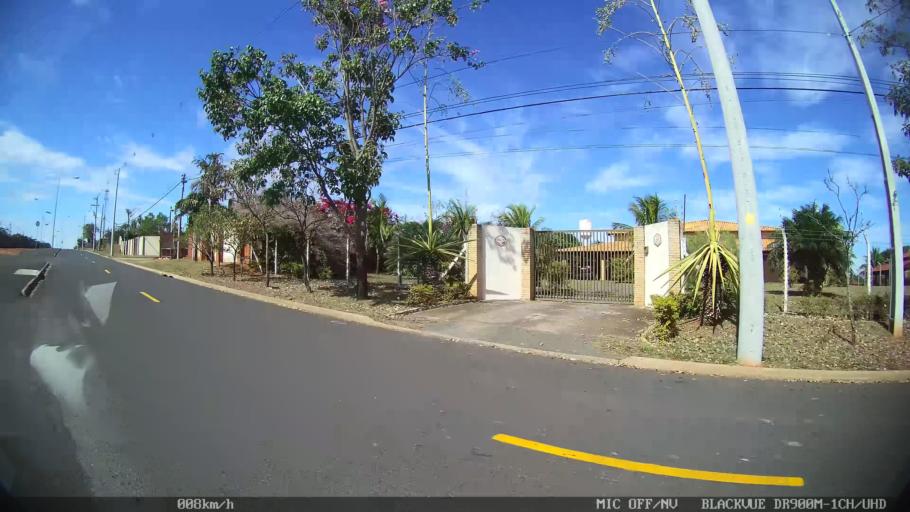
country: BR
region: Sao Paulo
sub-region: Bady Bassitt
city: Bady Bassitt
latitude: -20.8270
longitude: -49.4832
